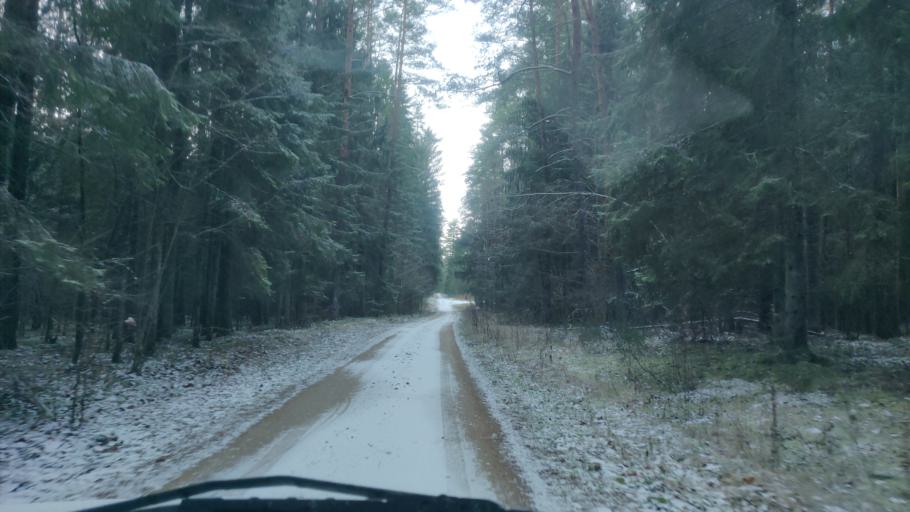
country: LT
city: Trakai
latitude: 54.5818
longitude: 24.9515
